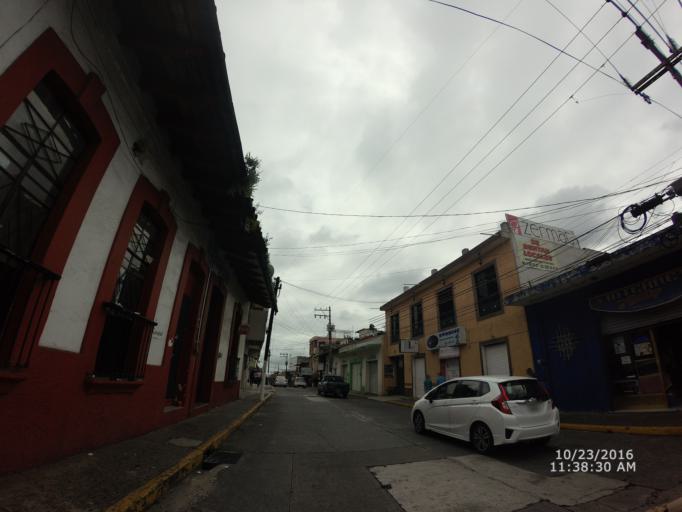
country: MX
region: Veracruz
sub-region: Xalapa
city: Xalapa de Enriquez
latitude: 19.5328
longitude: -96.9257
